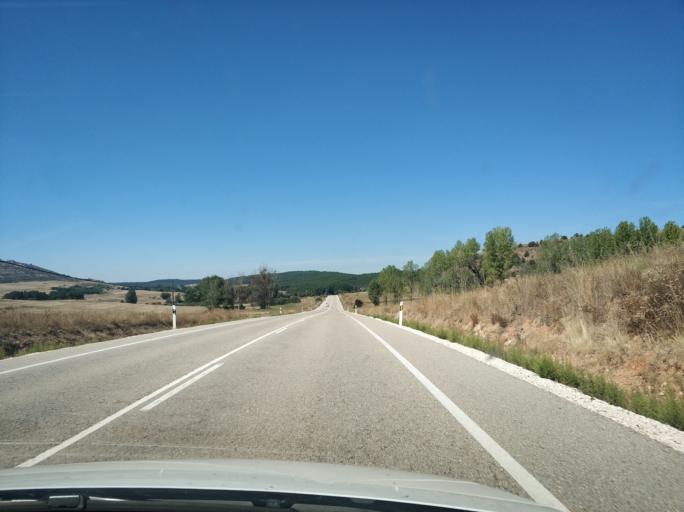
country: ES
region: Castille and Leon
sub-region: Provincia de Burgos
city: Hontoria del Pinar
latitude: 41.8527
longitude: -3.1808
